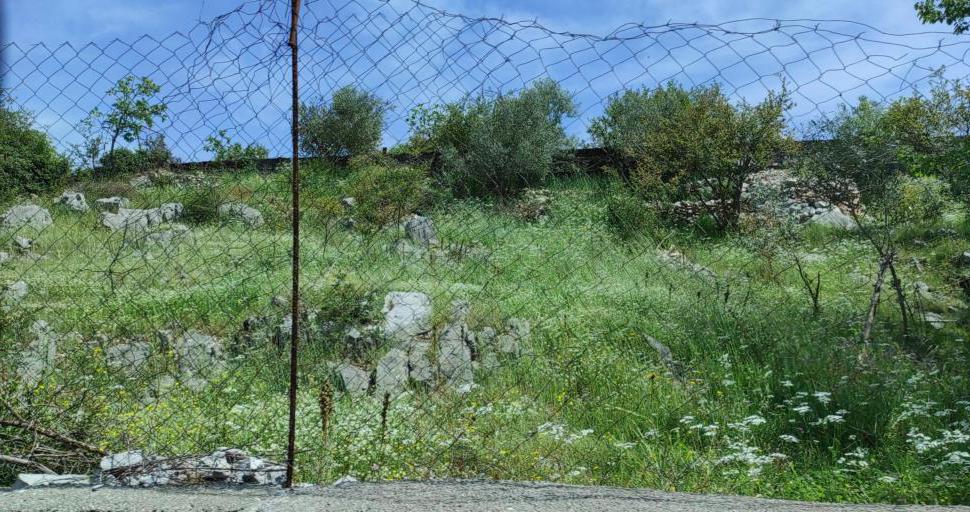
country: AL
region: Shkoder
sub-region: Rrethi i Malesia e Madhe
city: Gruemire
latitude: 42.1405
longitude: 19.5473
